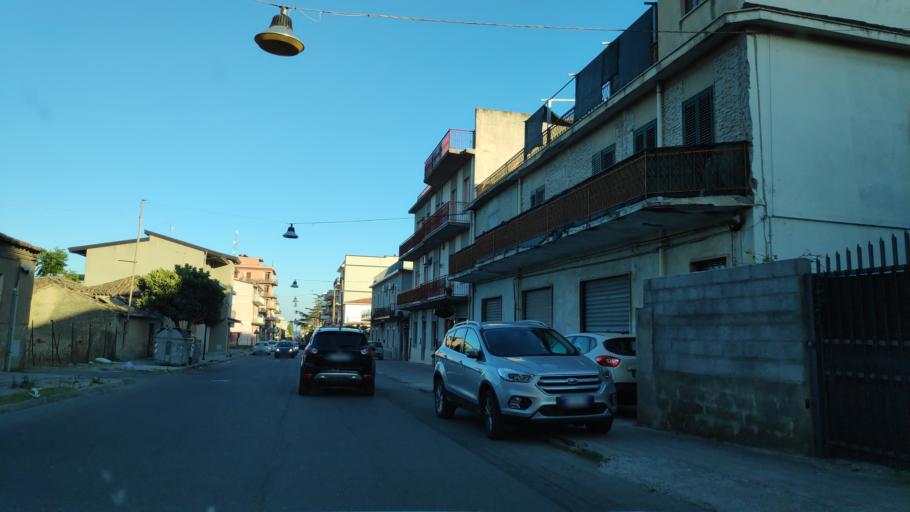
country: IT
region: Calabria
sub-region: Provincia di Reggio Calabria
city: Locri
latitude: 38.2393
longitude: 16.2546
